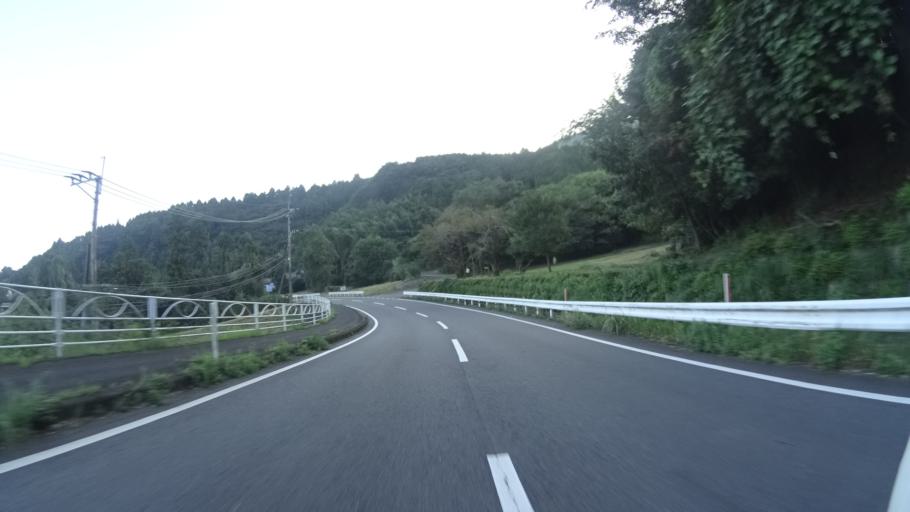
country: JP
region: Oita
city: Beppu
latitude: 33.3268
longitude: 131.4501
